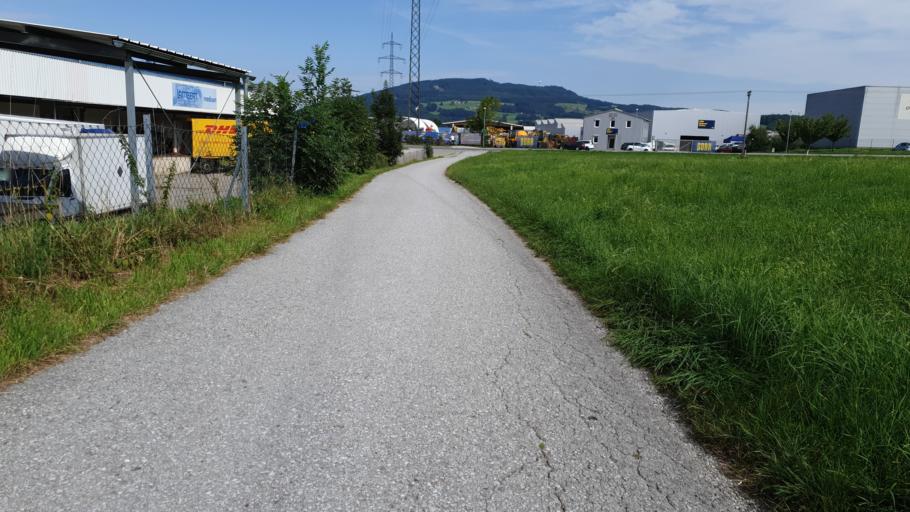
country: AT
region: Salzburg
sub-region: Politischer Bezirk Salzburg-Umgebung
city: Anthering
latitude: 47.8636
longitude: 13.0114
